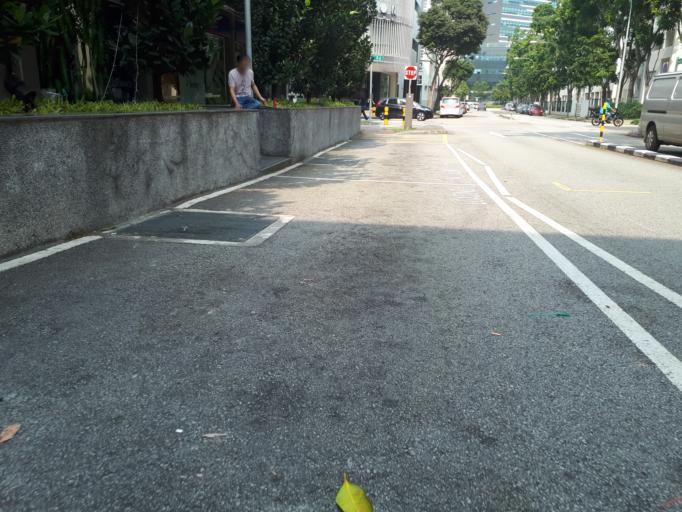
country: SG
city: Singapore
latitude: 1.3086
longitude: 103.8619
